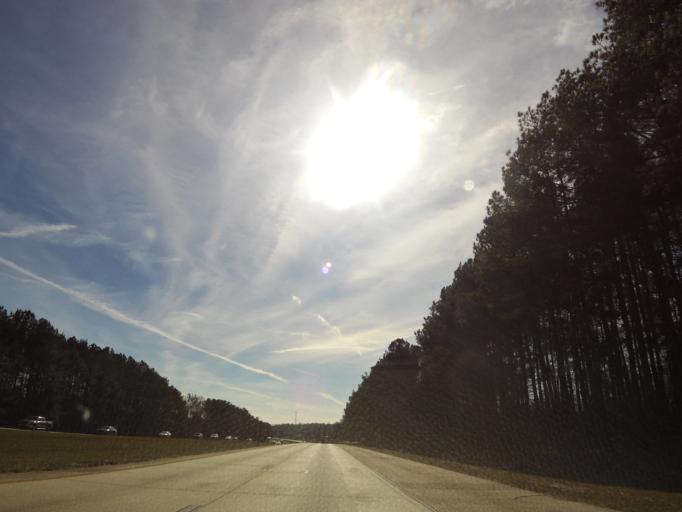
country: US
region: Georgia
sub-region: Troup County
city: Hogansville
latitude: 33.1768
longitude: -84.8616
